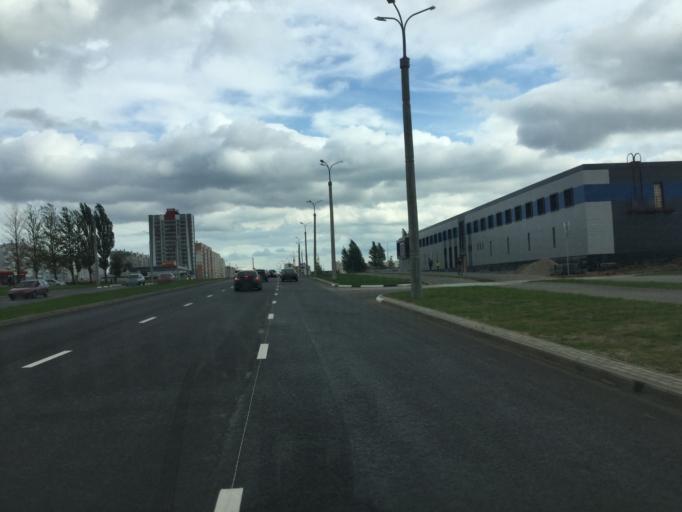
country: BY
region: Vitebsk
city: Vitebsk
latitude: 55.1669
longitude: 30.2506
